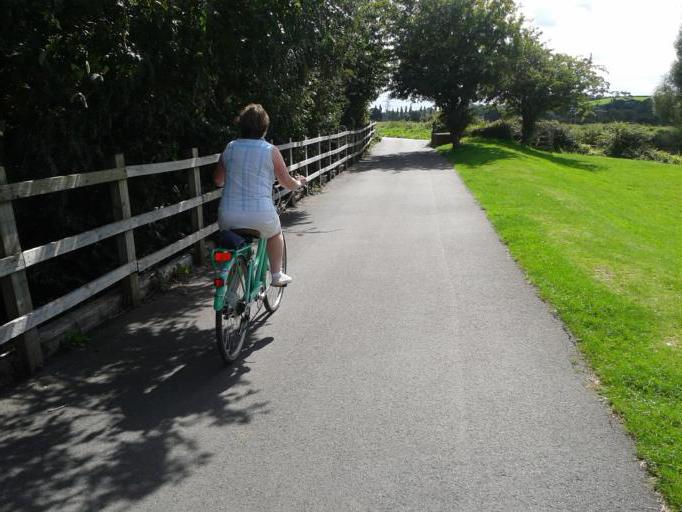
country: GB
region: England
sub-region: Devon
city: Exminster
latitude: 50.6993
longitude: -3.5113
